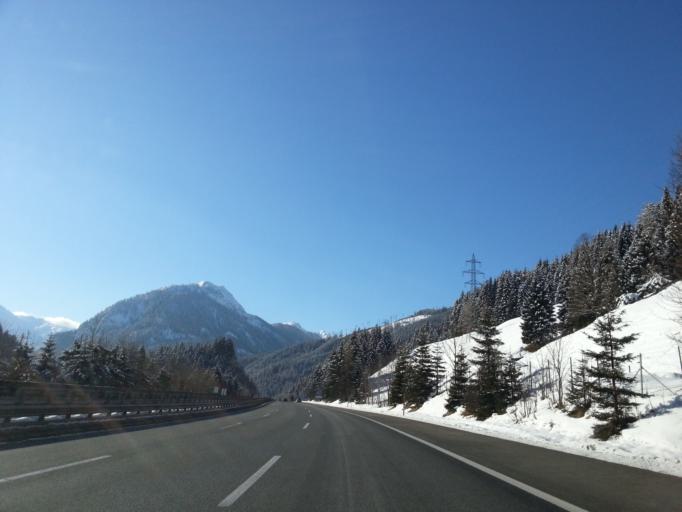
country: AT
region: Salzburg
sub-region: Politischer Bezirk Sankt Johann im Pongau
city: Flachau
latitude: 47.3080
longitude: 13.3930
